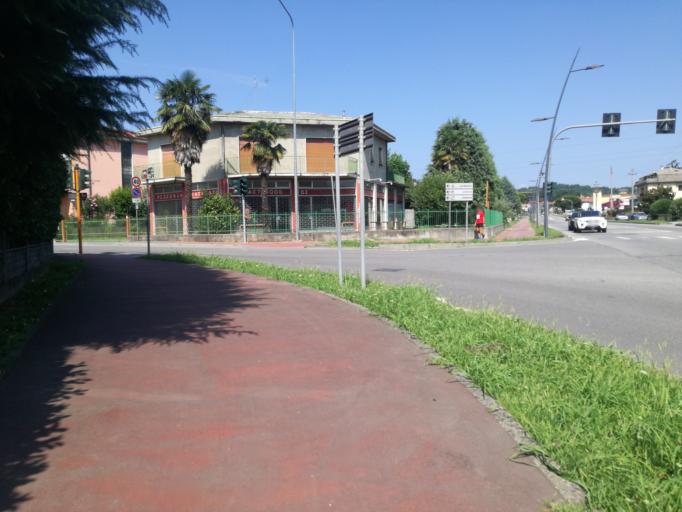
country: IT
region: Lombardy
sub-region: Provincia di Bergamo
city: Calusco d'Adda
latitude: 45.6869
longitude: 9.4823
